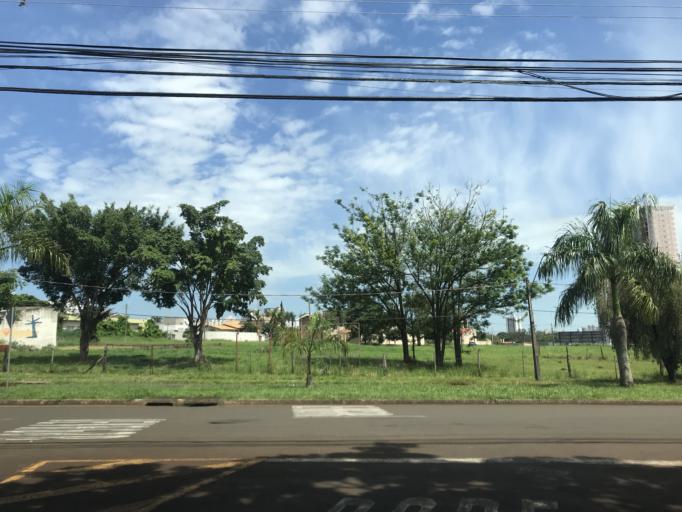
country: BR
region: Parana
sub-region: Londrina
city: Londrina
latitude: -23.3464
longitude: -51.1637
